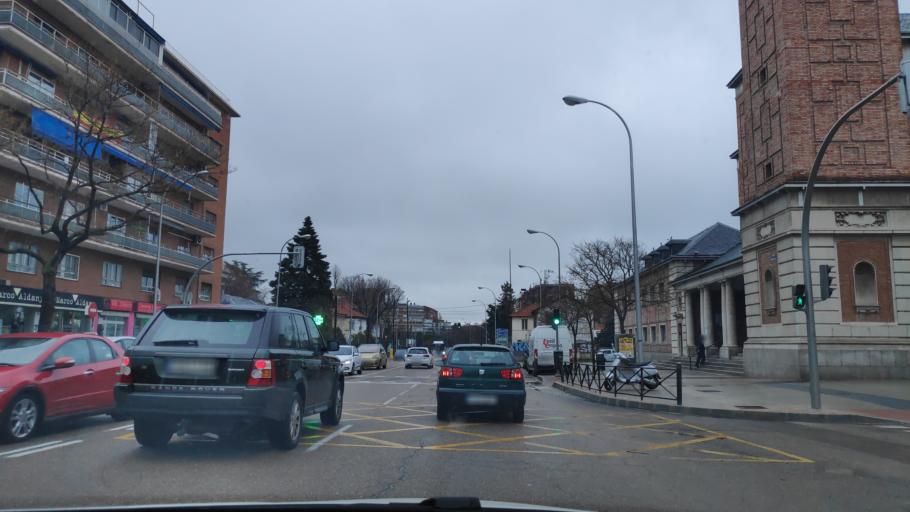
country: ES
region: Madrid
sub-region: Provincia de Madrid
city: Chamartin
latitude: 40.4524
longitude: -3.6691
